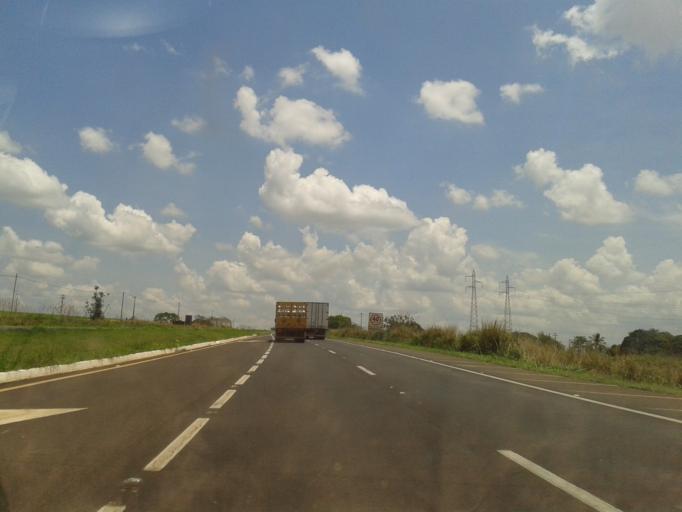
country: BR
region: Minas Gerais
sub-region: Uberlandia
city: Uberlandia
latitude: -18.8684
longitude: -48.5619
